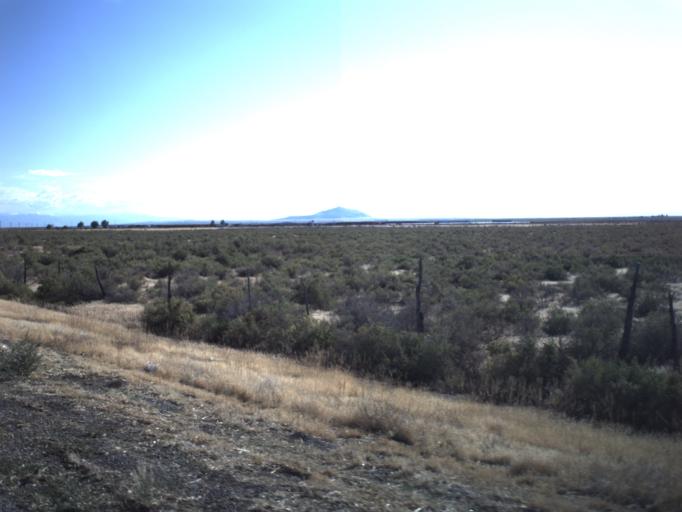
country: US
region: Utah
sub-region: Millard County
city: Delta
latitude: 39.3242
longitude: -112.4838
